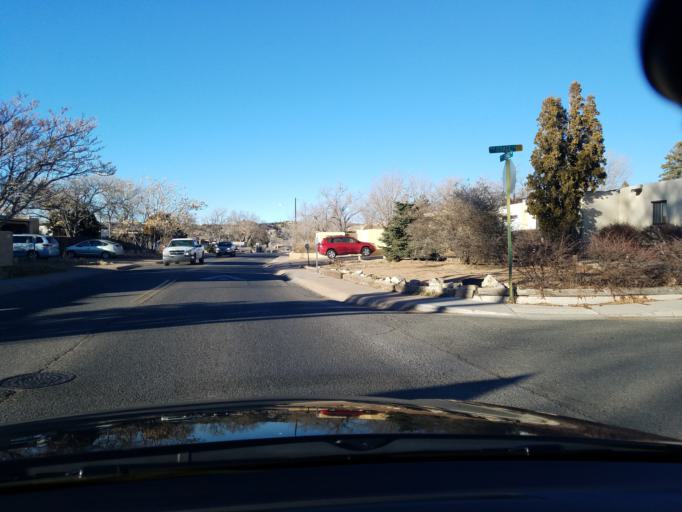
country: US
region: New Mexico
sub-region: Santa Fe County
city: Agua Fria
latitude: 35.6699
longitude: -105.9806
